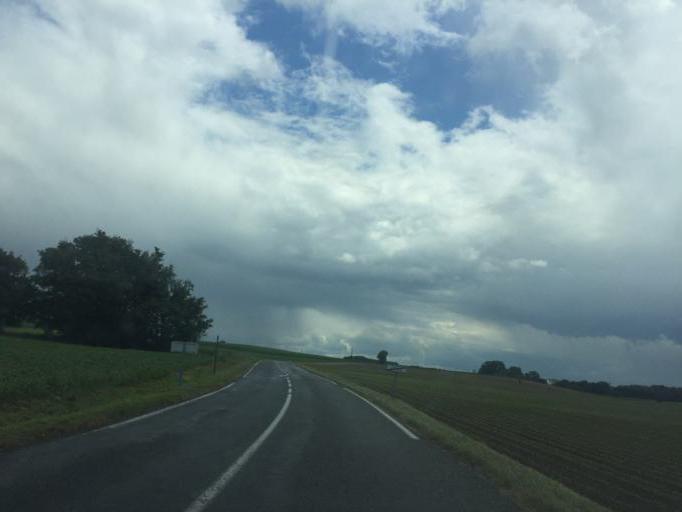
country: FR
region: Rhone-Alpes
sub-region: Departement du Rhone
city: Jons
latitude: 45.8008
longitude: 5.0889
